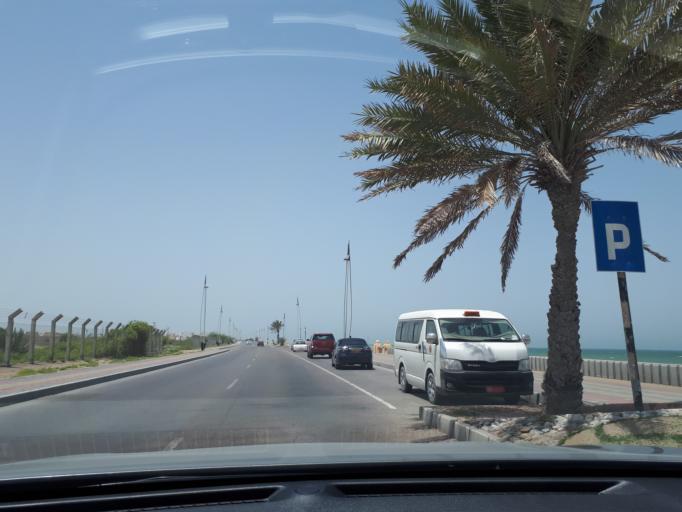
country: OM
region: Muhafazat Masqat
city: As Sib al Jadidah
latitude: 23.6504
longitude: 58.2332
